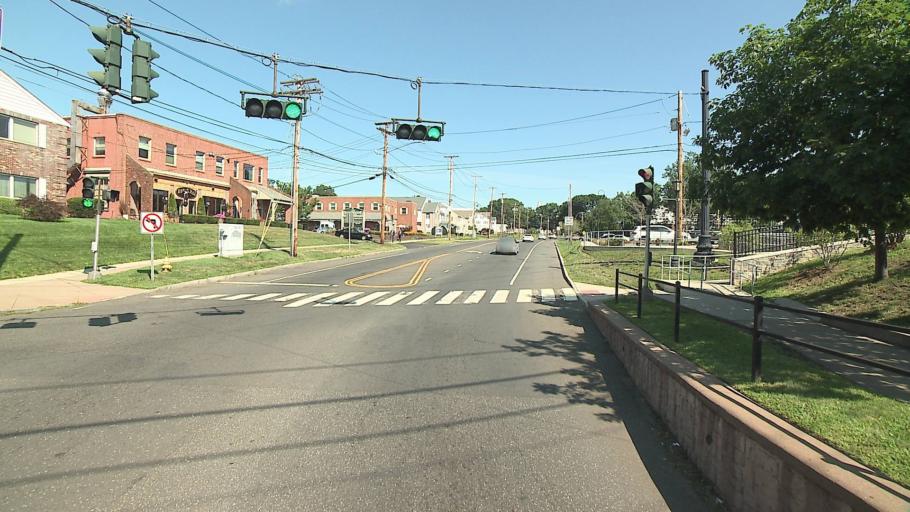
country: US
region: Connecticut
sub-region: Fairfield County
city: Stratford
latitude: 41.1943
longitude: -73.1317
